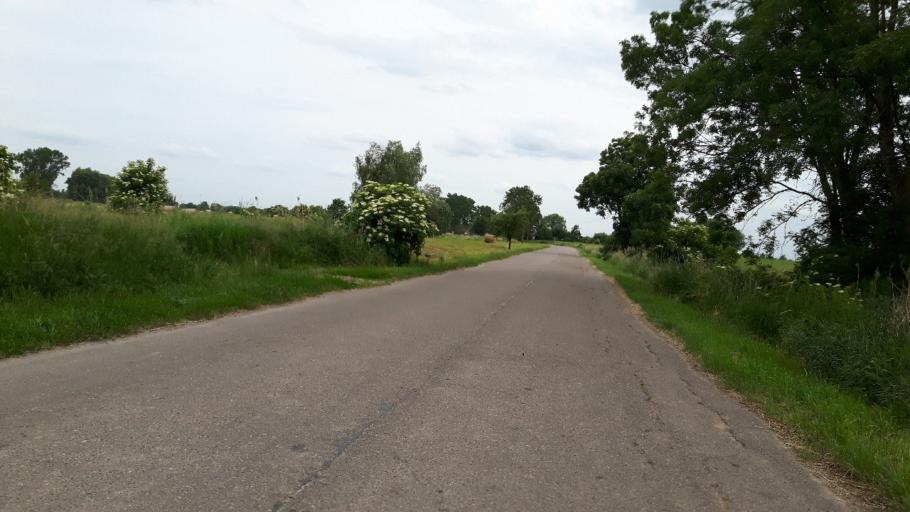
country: PL
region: Pomeranian Voivodeship
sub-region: Powiat nowodworski
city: Sztutowo
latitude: 54.2484
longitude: 19.2383
